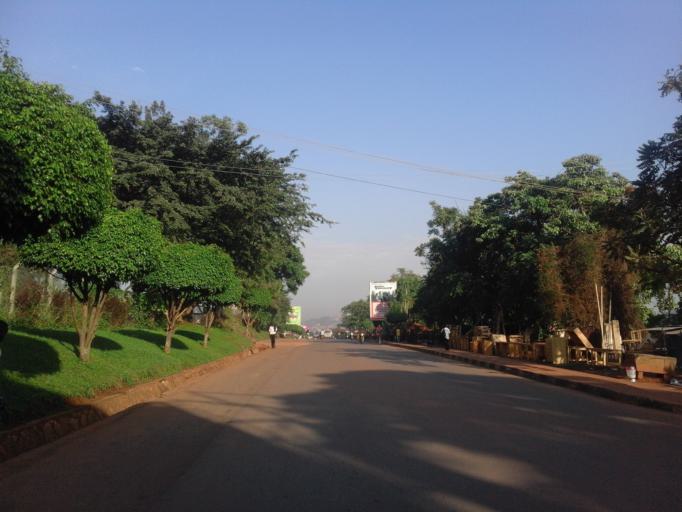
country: UG
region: Central Region
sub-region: Kampala District
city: Kampala
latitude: 0.3016
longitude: 32.5906
